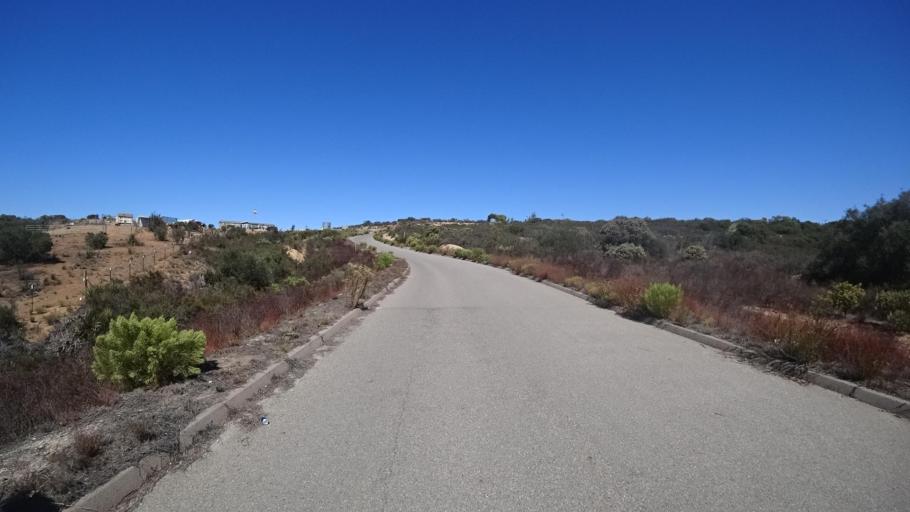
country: US
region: California
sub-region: San Diego County
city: Alpine
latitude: 32.7601
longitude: -116.7729
